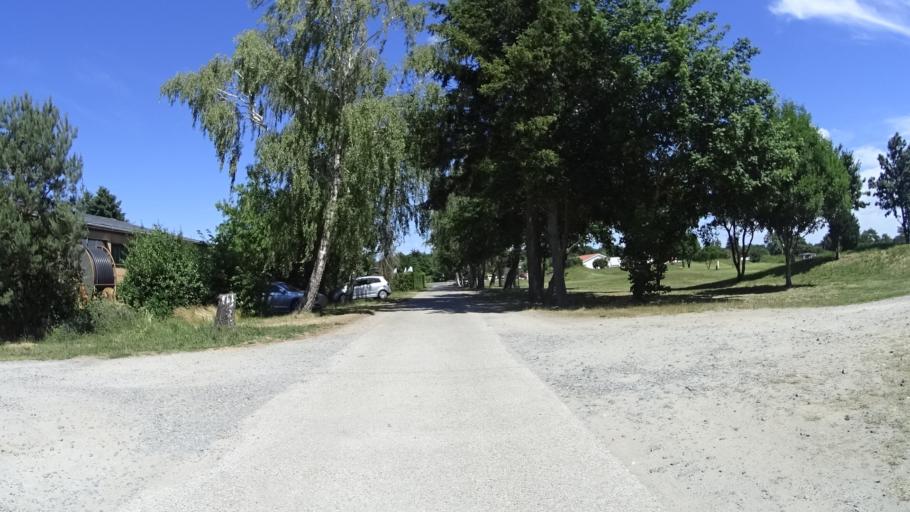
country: DE
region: Hesse
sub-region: Regierungsbezirk Darmstadt
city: Buttelborn
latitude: 49.9416
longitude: 8.5500
